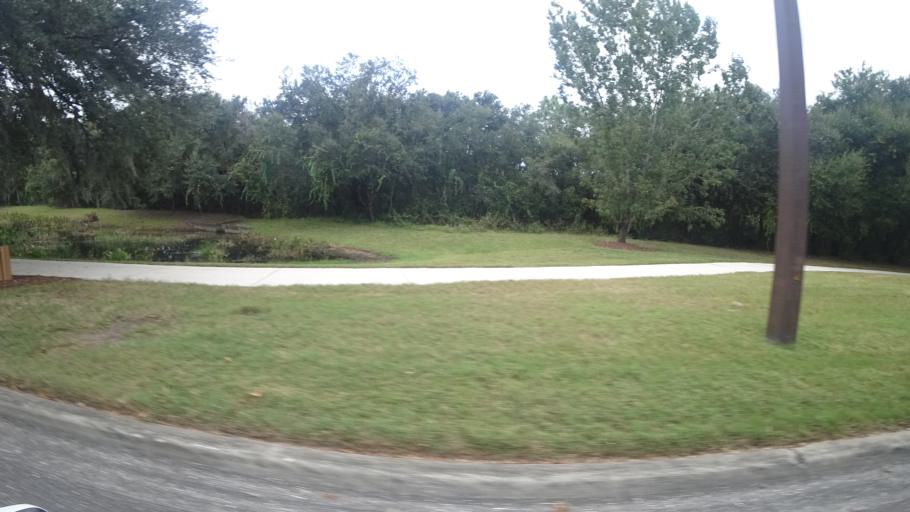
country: US
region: Florida
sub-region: Sarasota County
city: The Meadows
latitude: 27.4220
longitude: -82.4259
